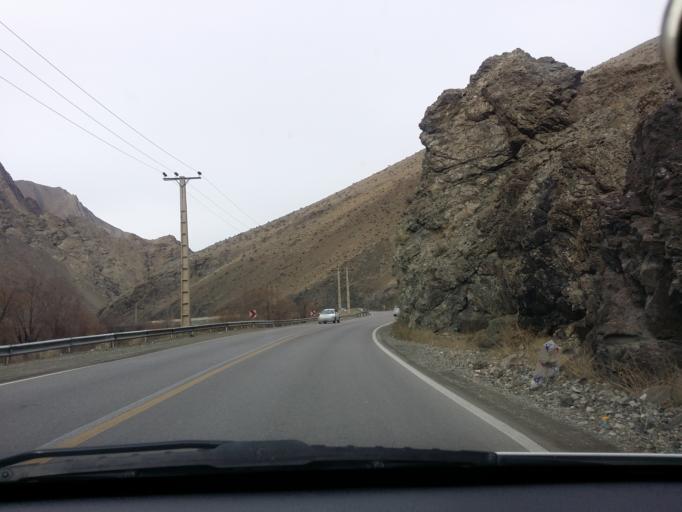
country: IR
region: Tehran
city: Tajrish
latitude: 36.0148
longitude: 51.2859
